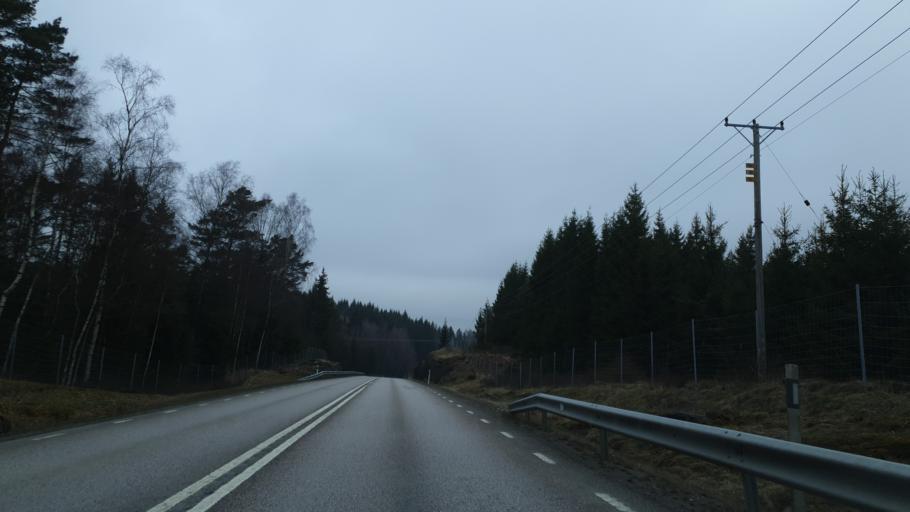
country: SE
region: Vaestra Goetaland
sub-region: Harryda Kommun
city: Hindas
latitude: 57.6378
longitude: 12.4075
